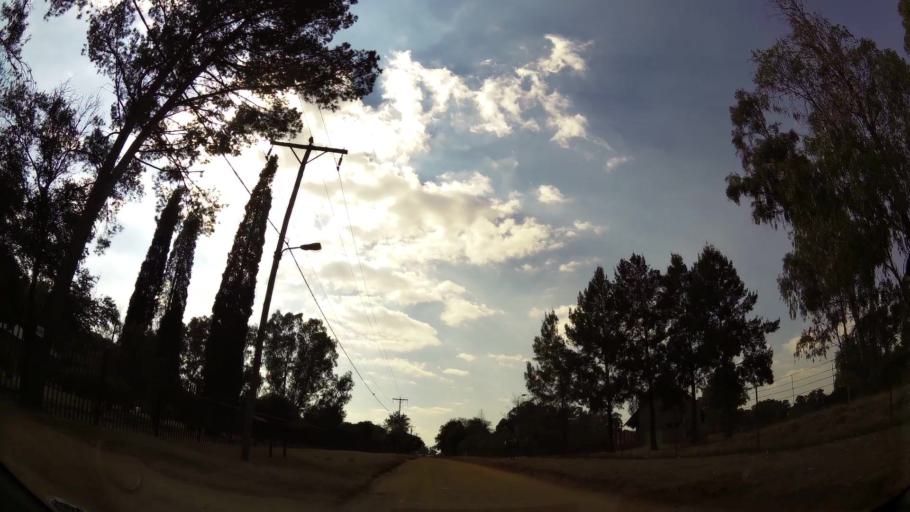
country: ZA
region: Gauteng
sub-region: Ekurhuleni Metropolitan Municipality
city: Benoni
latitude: -26.0927
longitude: 28.3563
